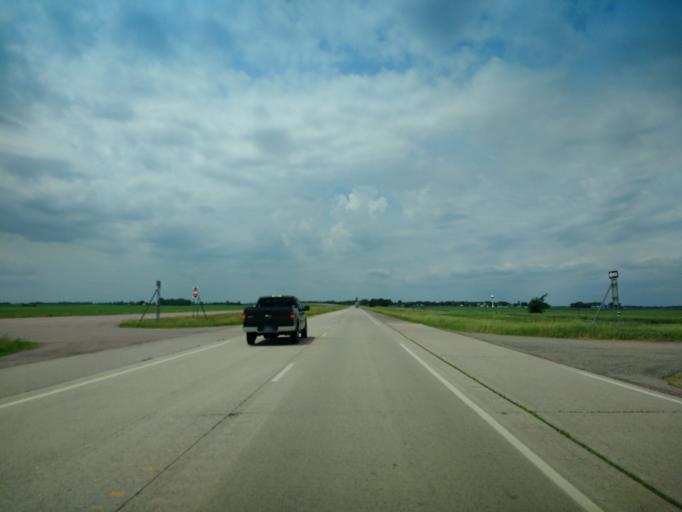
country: US
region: Minnesota
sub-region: Watonwan County
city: Saint James
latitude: 43.9625
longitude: -94.7588
